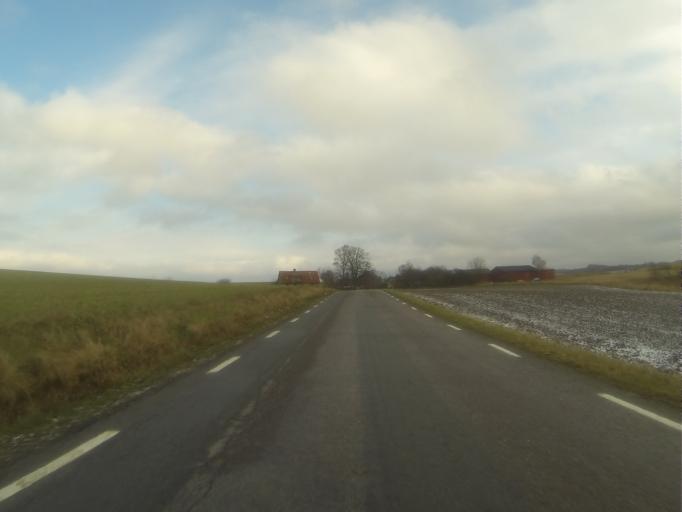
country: SE
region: Skane
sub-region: Svedala Kommun
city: Klagerup
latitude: 55.5925
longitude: 13.2980
